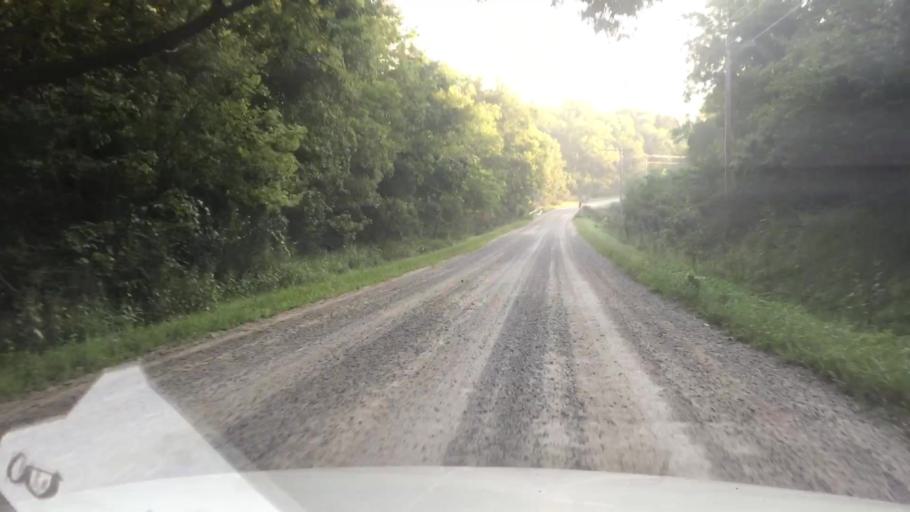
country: US
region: Iowa
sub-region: Story County
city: Huxley
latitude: 41.9049
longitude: -93.5792
